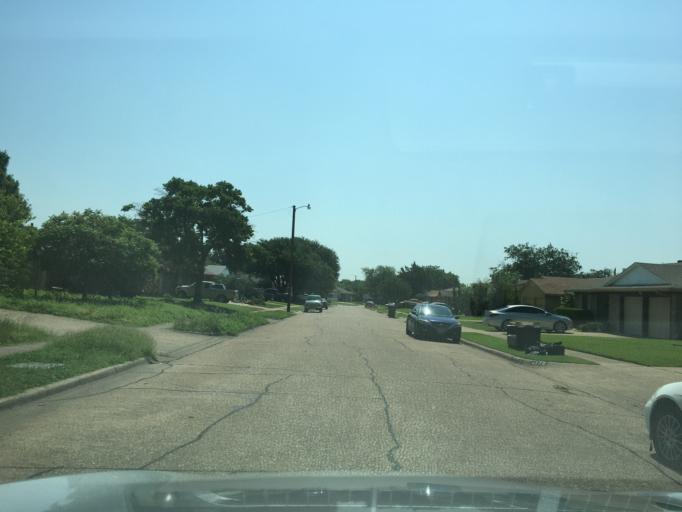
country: US
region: Texas
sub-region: Dallas County
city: Richardson
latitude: 32.9219
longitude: -96.6983
